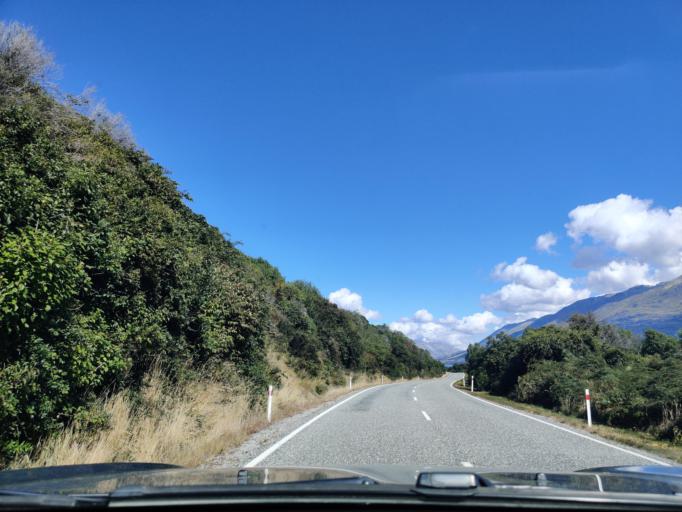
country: NZ
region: Otago
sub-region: Queenstown-Lakes District
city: Queenstown
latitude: -44.9715
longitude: 168.4373
